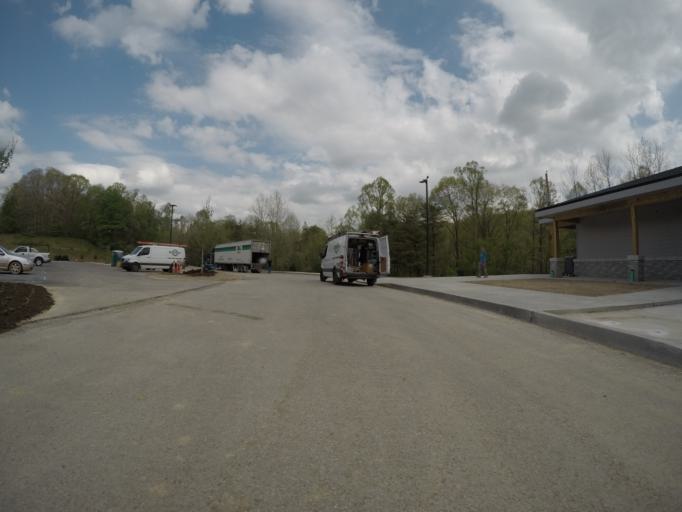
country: US
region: West Virginia
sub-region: Kanawha County
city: Alum Creek
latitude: 38.2675
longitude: -81.7945
